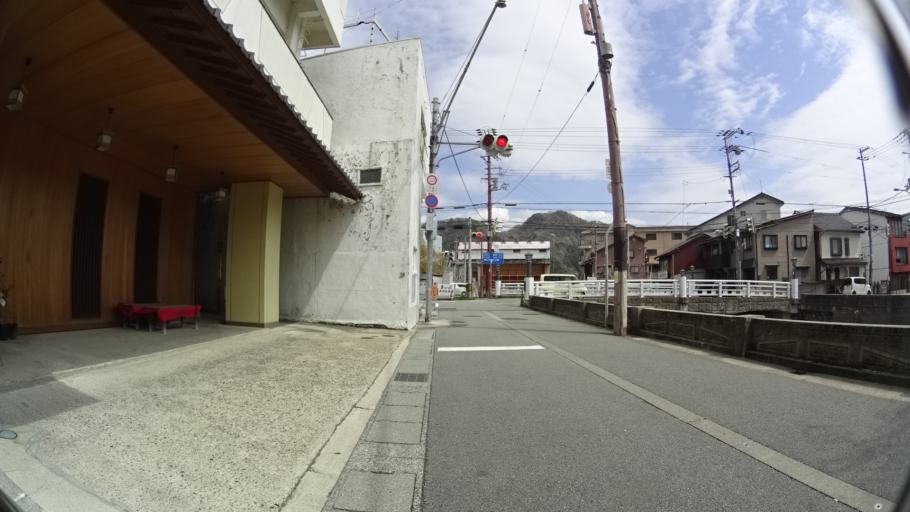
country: JP
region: Hyogo
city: Toyooka
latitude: 35.6192
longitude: 134.8075
